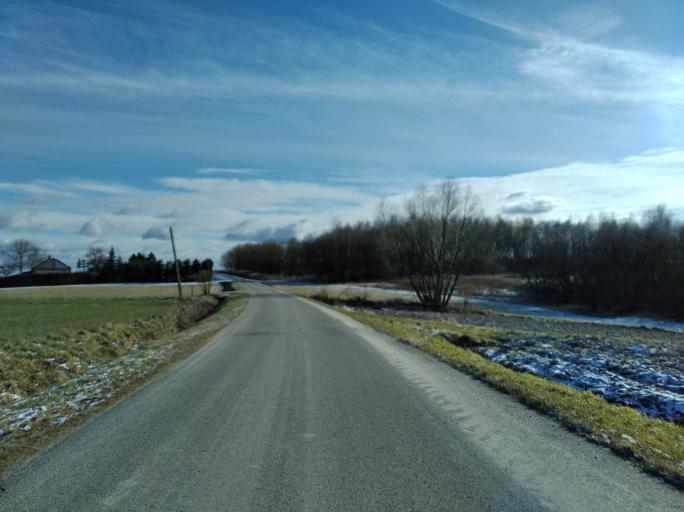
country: PL
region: Subcarpathian Voivodeship
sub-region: Powiat ropczycko-sedziszowski
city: Wielopole Skrzynskie
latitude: 49.9117
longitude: 21.6391
